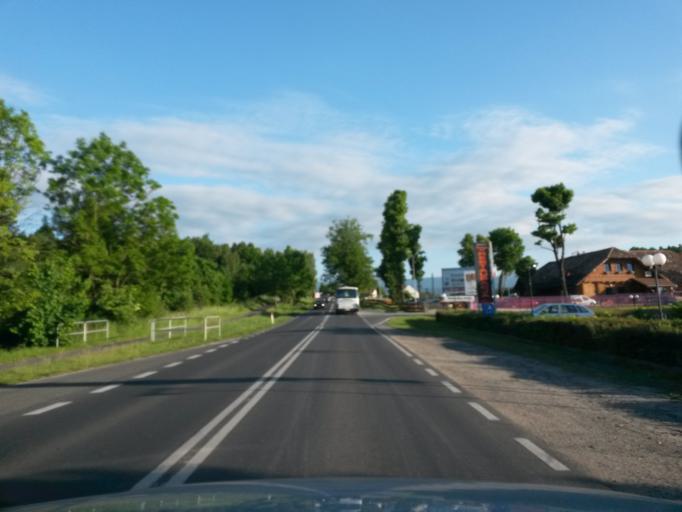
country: PL
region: Lower Silesian Voivodeship
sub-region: Jelenia Gora
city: Jelenia Gora
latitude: 50.8787
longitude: 15.7589
